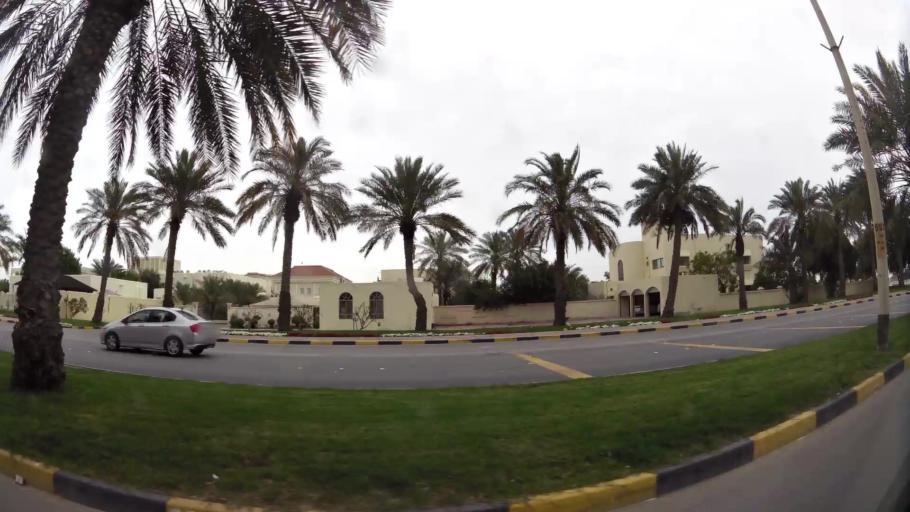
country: BH
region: Northern
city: Ar Rifa'
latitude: 26.1202
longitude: 50.5366
